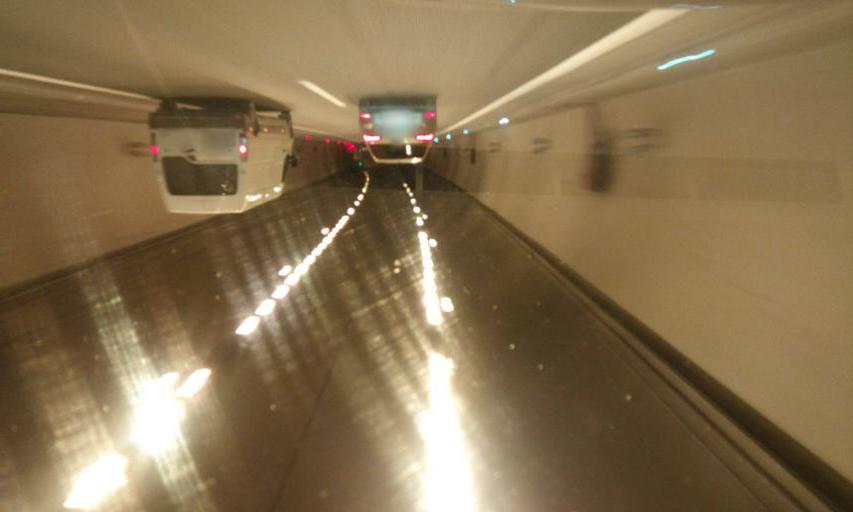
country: TR
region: Kocaeli
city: Izmit
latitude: 40.7755
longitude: 29.8991
